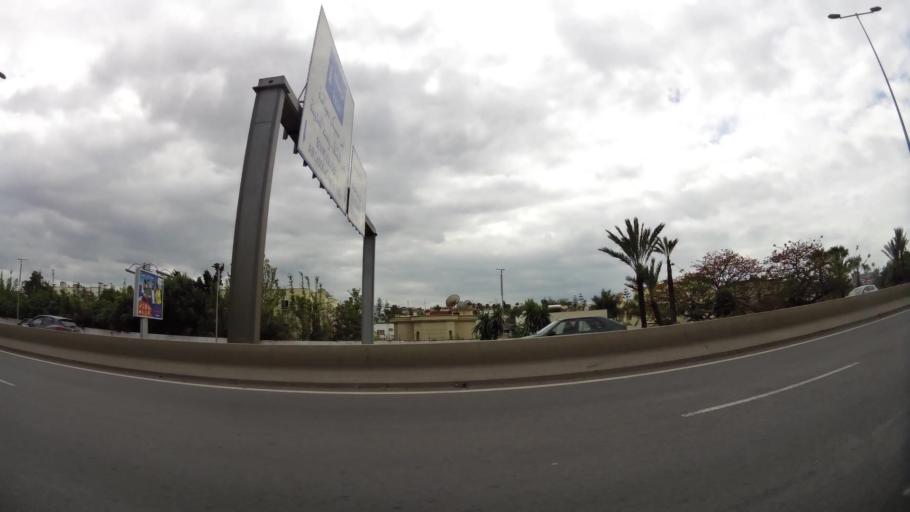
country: MA
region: Grand Casablanca
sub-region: Casablanca
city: Casablanca
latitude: 33.5521
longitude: -7.6309
